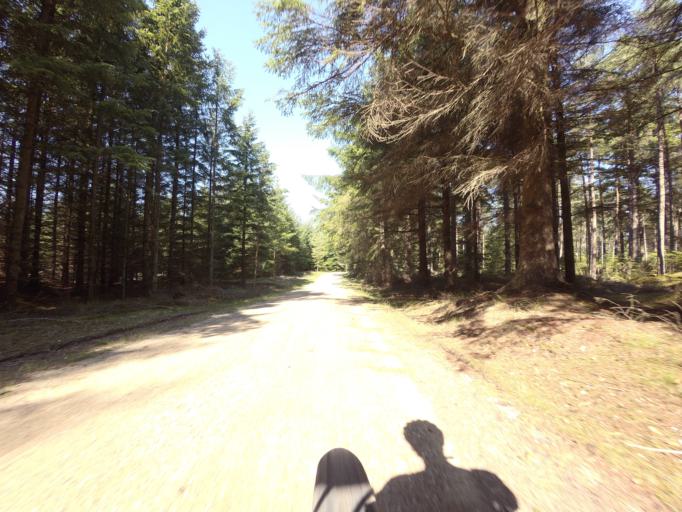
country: DK
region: North Denmark
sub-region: Hjorring Kommune
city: Hirtshals
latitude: 57.5833
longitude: 10.0655
